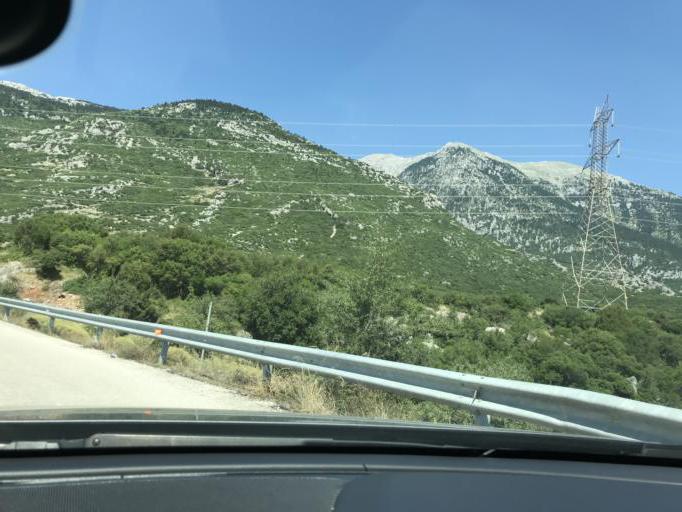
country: GR
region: Central Greece
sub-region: Nomos Voiotias
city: Distomo
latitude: 38.5092
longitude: 22.7072
